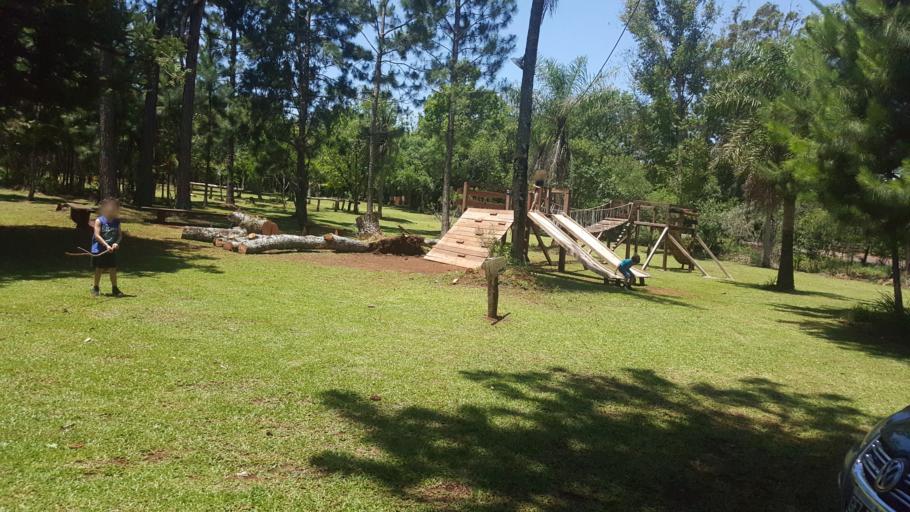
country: AR
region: Misiones
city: Garupa
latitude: -27.5038
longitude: -55.8536
